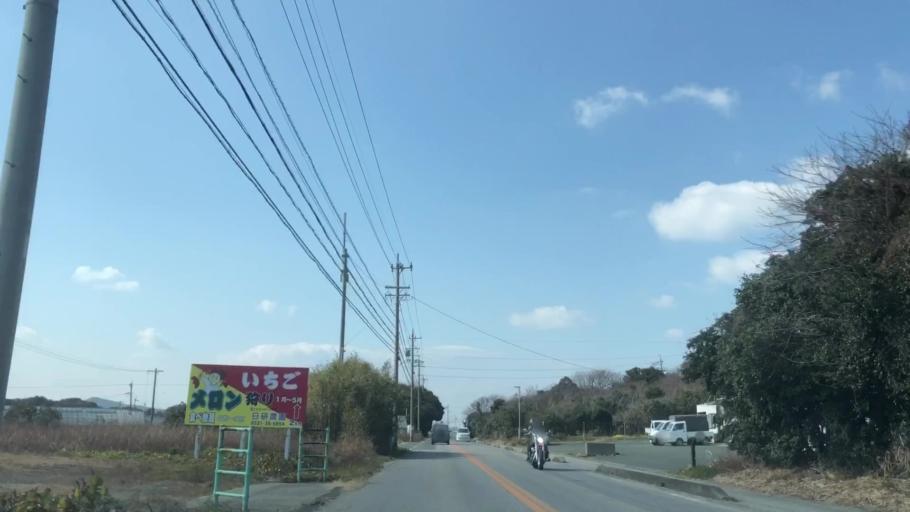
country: JP
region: Aichi
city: Tahara
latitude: 34.5908
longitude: 137.1047
